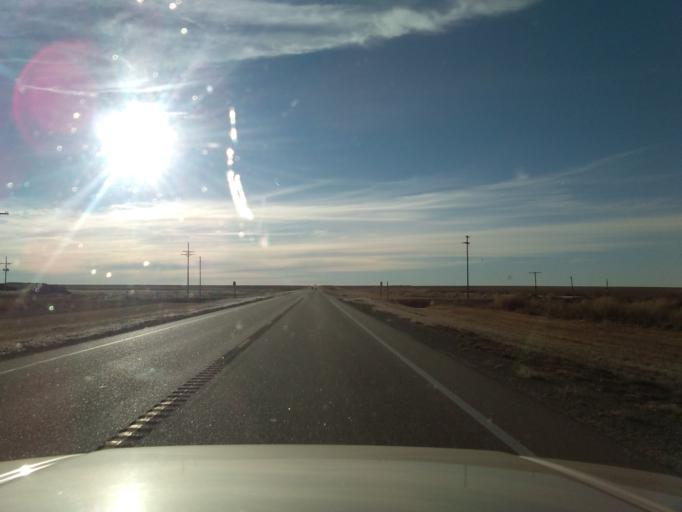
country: US
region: Kansas
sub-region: Sheridan County
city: Hoxie
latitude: 39.5349
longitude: -100.5894
